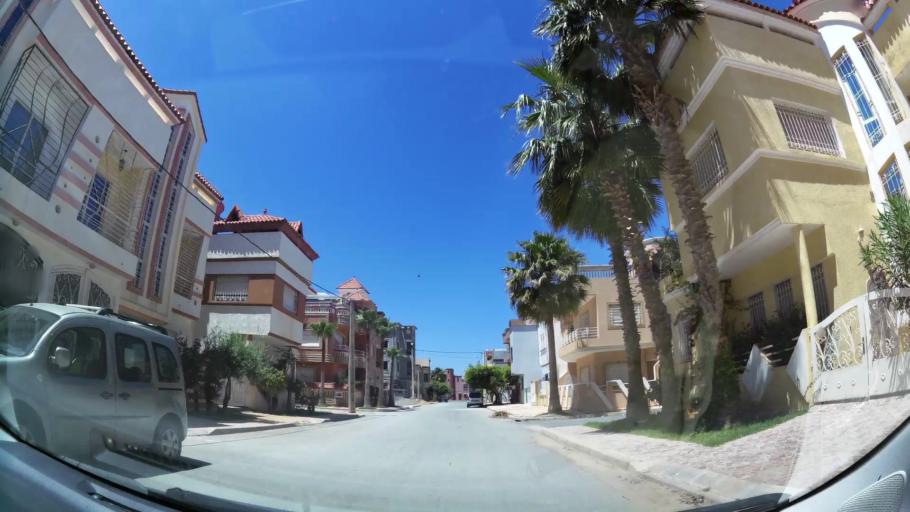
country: MA
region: Oriental
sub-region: Berkane-Taourirt
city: Madagh
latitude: 35.0829
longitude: -2.2282
